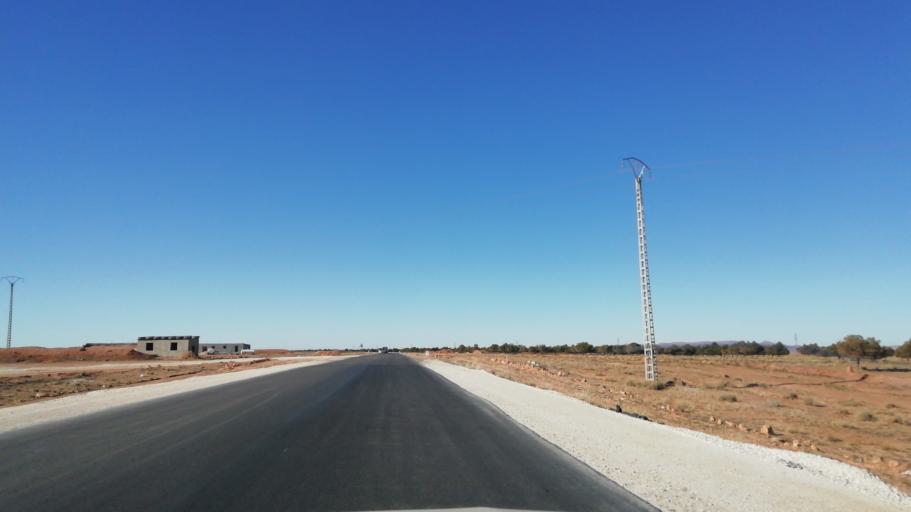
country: DZ
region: El Bayadh
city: El Bayadh
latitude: 33.6663
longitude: 0.9241
